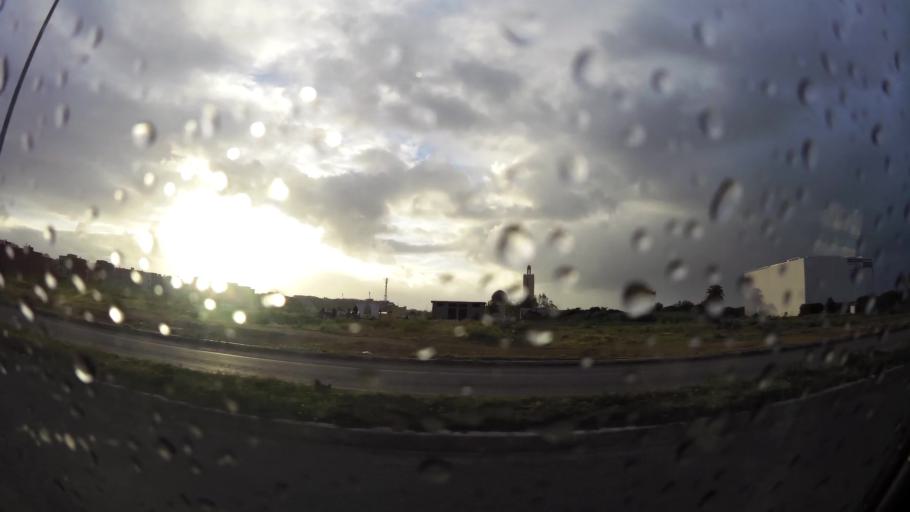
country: MA
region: Doukkala-Abda
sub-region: El-Jadida
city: El Jadida
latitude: 33.2356
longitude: -8.4837
